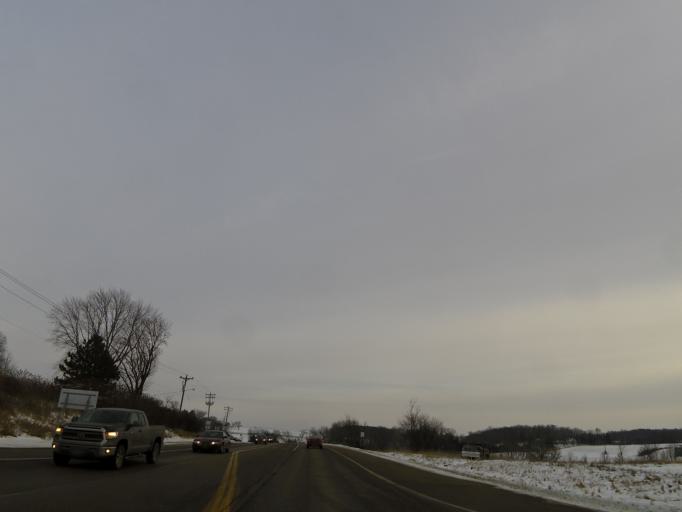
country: US
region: Minnesota
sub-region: Hennepin County
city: Saint Bonifacius
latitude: 44.8999
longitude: -93.7311
